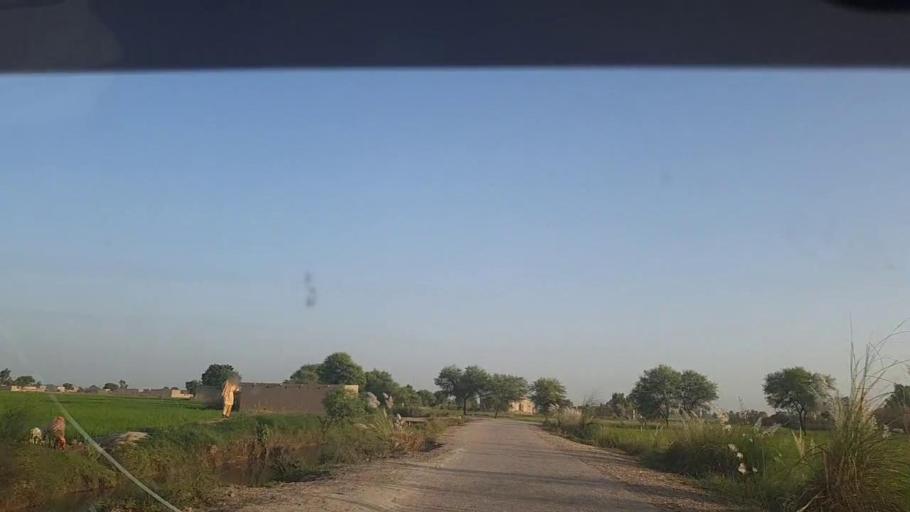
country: PK
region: Sindh
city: Thul
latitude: 28.1213
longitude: 68.8952
